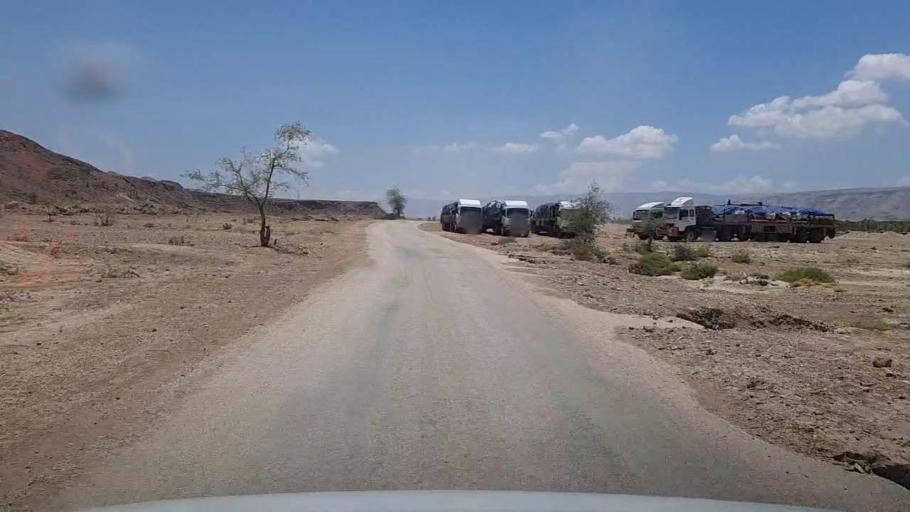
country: PK
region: Sindh
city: Bhan
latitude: 26.2996
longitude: 67.5348
